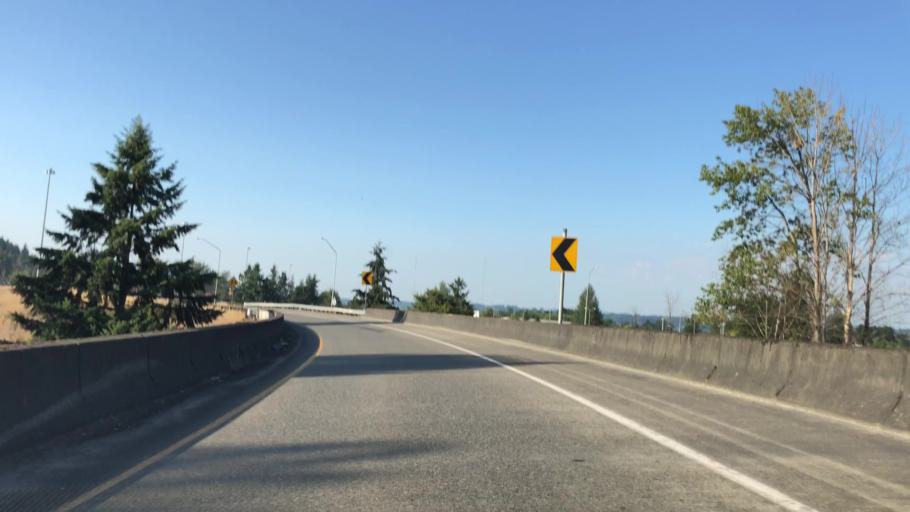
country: US
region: Washington
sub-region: King County
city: Algona
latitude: 47.2997
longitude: -122.2528
